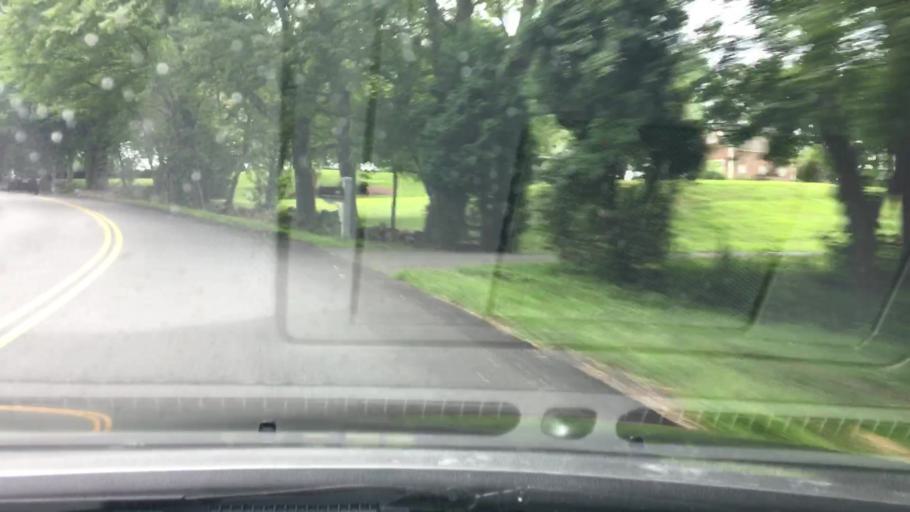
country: US
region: Rhode Island
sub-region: Providence County
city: Cumberland Hill
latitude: 42.0237
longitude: -71.4532
